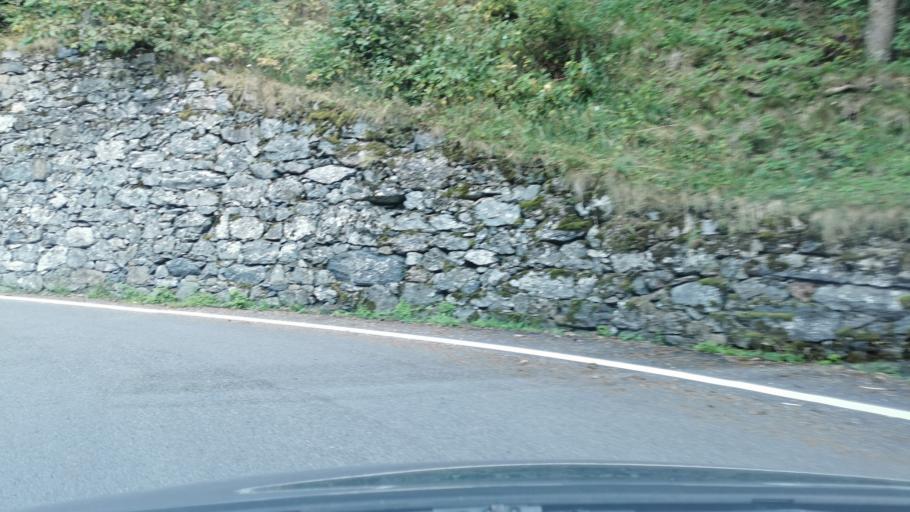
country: IT
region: Piedmont
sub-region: Provincia di Torino
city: Usseglio
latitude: 45.2224
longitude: 7.1979
